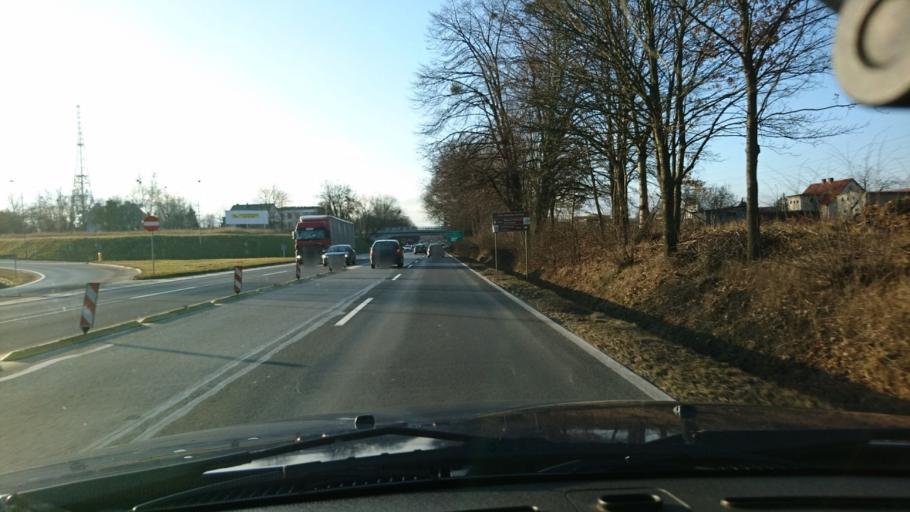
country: PL
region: Silesian Voivodeship
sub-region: Gliwice
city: Gliwice
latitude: 50.3146
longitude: 18.6963
